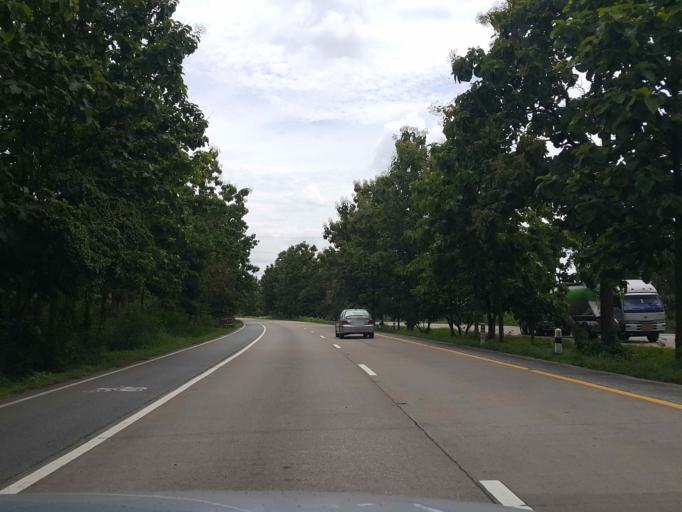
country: TH
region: Lamphun
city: Mae Tha
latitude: 18.4789
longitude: 99.1276
